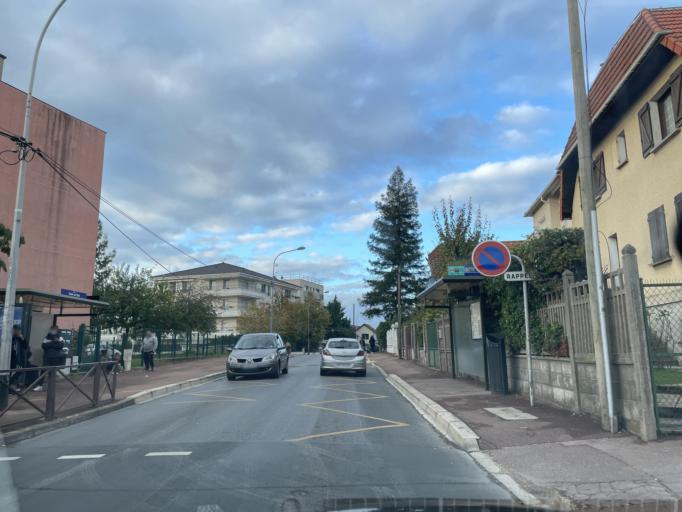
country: FR
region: Ile-de-France
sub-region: Departement du Val-de-Marne
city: Creteil
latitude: 48.7852
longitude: 2.4630
